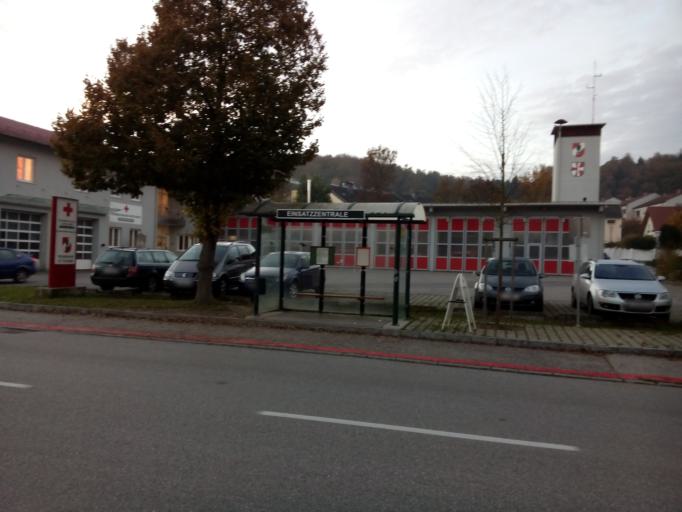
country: AT
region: Upper Austria
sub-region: Politischer Bezirk Linz-Land
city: Sankt Florian
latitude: 48.2043
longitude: 14.3723
